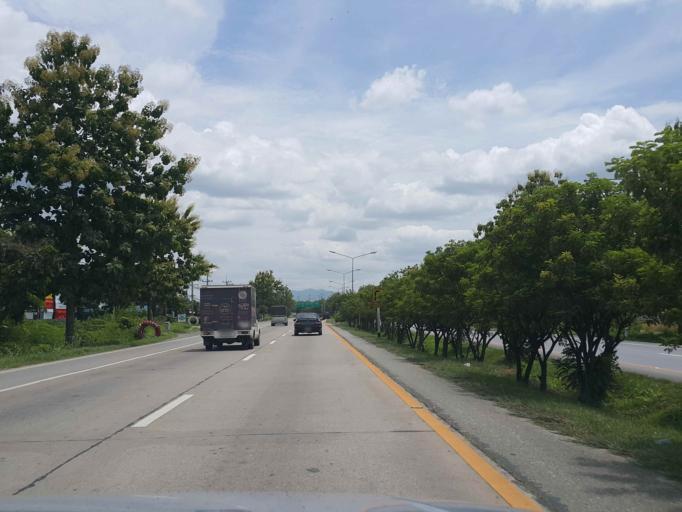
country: TH
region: Lamphun
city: Lamphun
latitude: 18.5615
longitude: 99.0455
